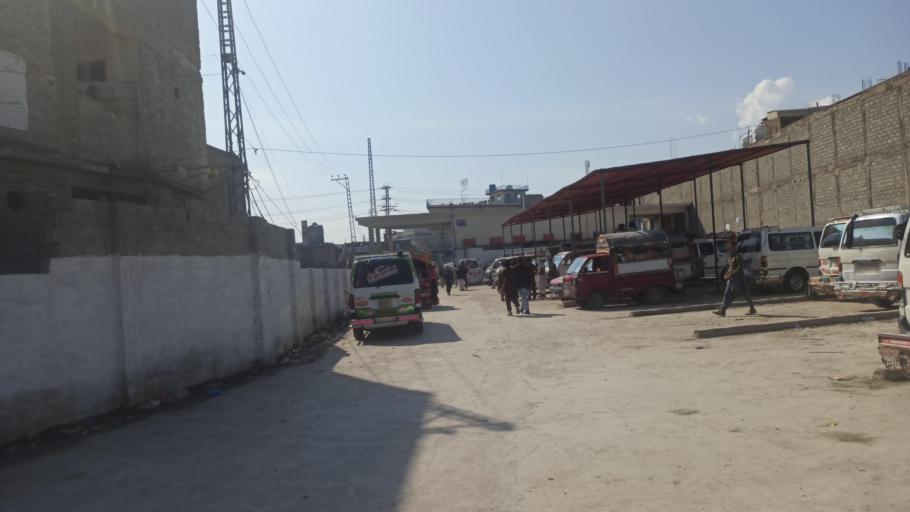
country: PK
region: Khyber Pakhtunkhwa
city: Mingora
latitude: 34.7890
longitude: 72.3504
